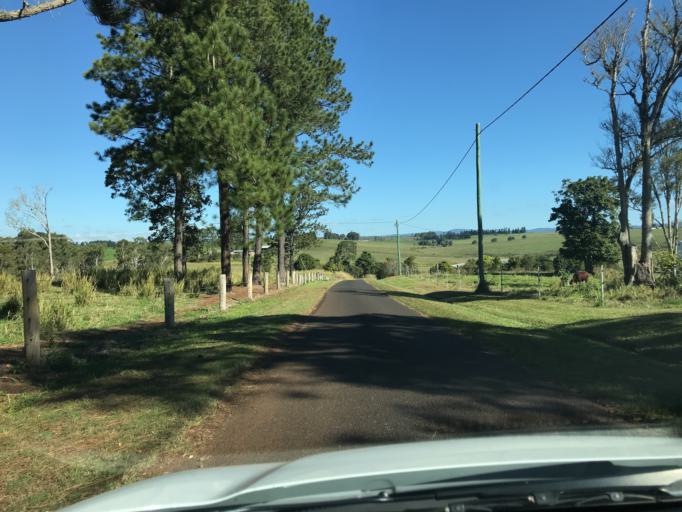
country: AU
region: Queensland
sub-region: Tablelands
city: Atherton
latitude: -17.2936
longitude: 145.5446
